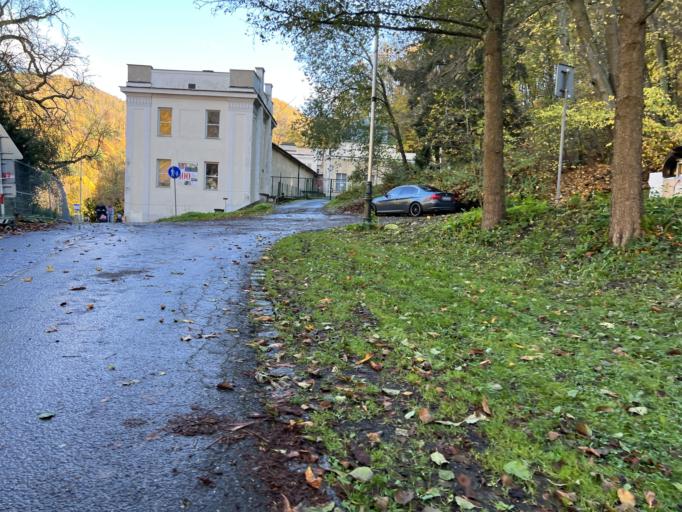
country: CZ
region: Karlovarsky
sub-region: Okres Karlovy Vary
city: Karlovy Vary
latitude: 50.2177
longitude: 12.8861
